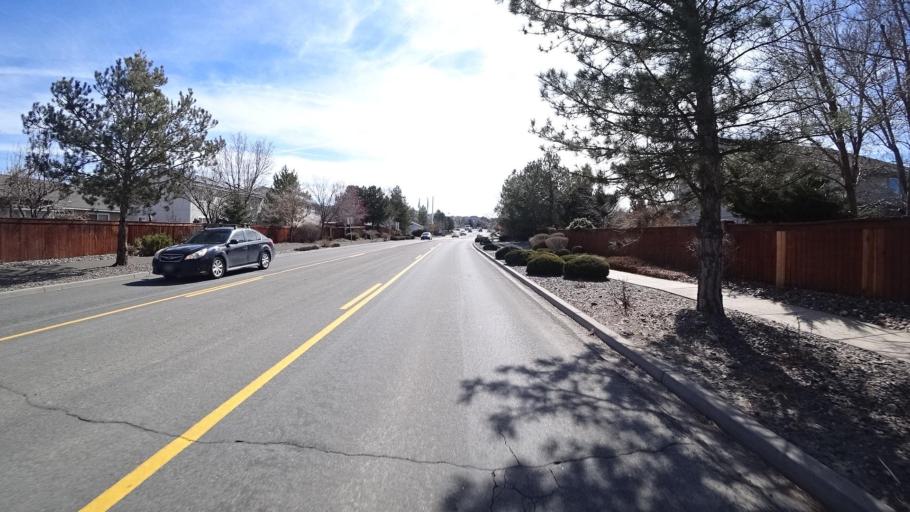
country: US
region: Nevada
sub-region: Washoe County
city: Sun Valley
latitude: 39.5873
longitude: -119.7185
